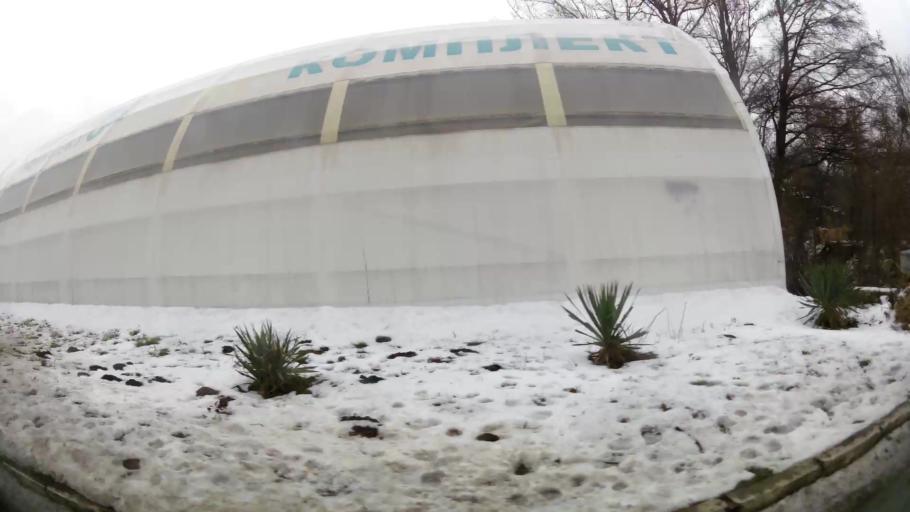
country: BG
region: Sofia-Capital
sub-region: Stolichna Obshtina
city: Sofia
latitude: 42.6529
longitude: 23.2948
